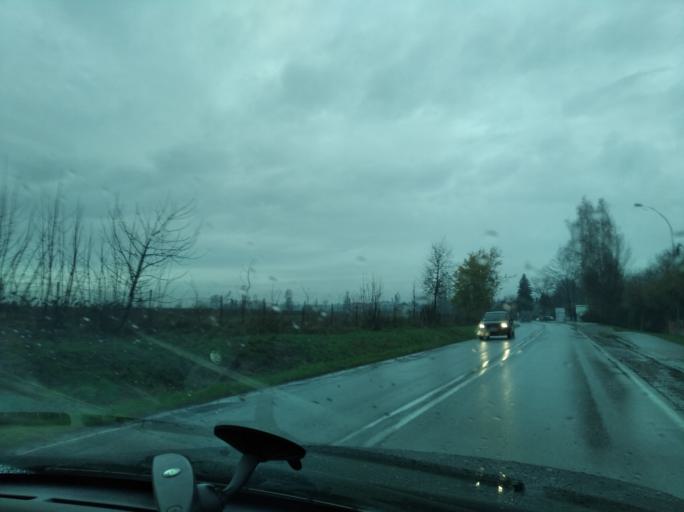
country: PL
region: Subcarpathian Voivodeship
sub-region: Powiat lancucki
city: Albigowa
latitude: 50.0305
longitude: 22.2283
